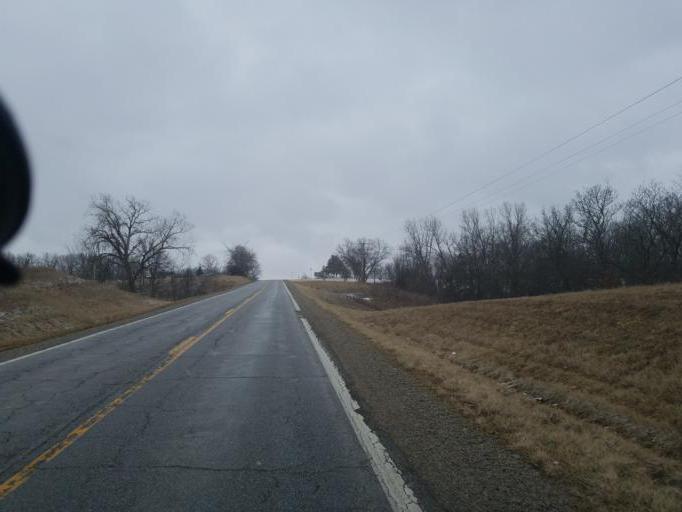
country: US
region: Missouri
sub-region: Putnam County
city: Unionville
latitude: 40.5261
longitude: -93.0143
